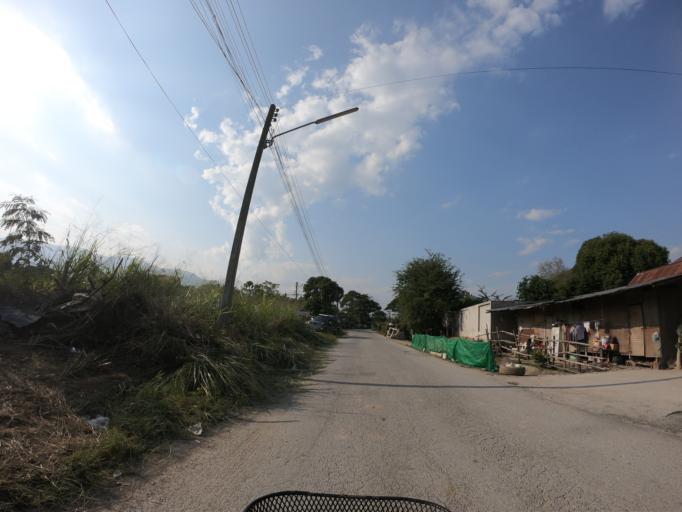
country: TH
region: Chiang Mai
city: Chiang Mai
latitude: 18.8330
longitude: 98.9898
